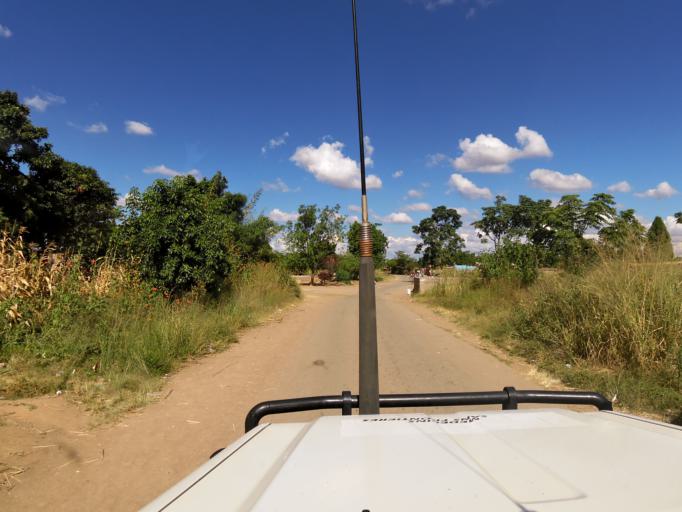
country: ZW
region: Harare
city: Epworth
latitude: -17.8704
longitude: 31.1363
